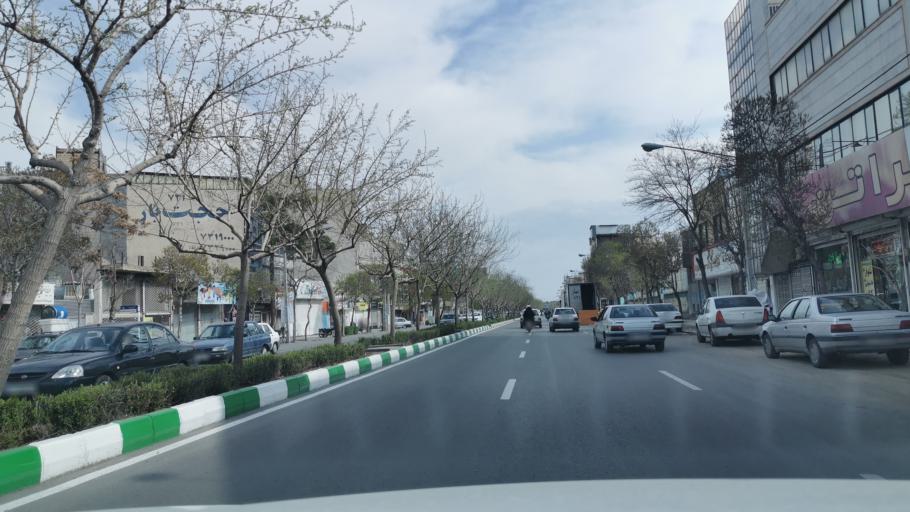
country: IR
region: Razavi Khorasan
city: Mashhad
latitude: 36.3151
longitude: 59.6104
